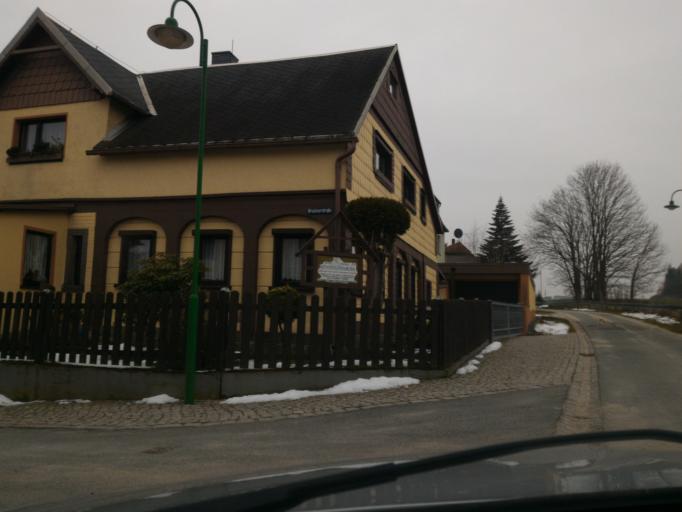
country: DE
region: Saxony
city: Neugersdorf
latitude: 50.9763
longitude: 14.5982
